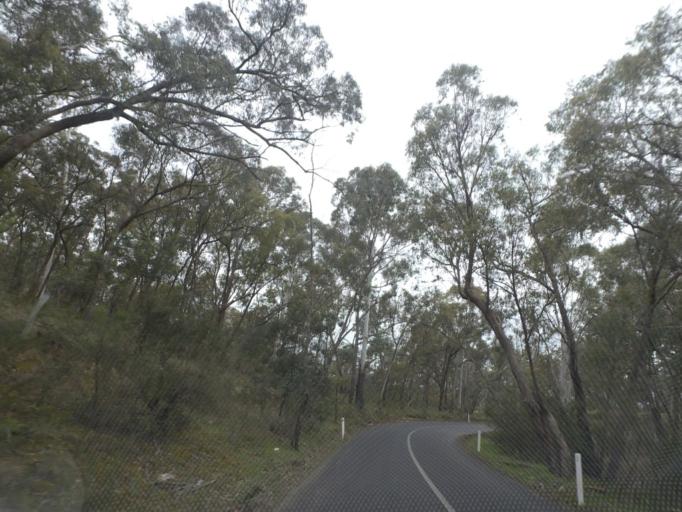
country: AU
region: Victoria
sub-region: Nillumbik
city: Hurstbridge
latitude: -37.6677
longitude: 145.2558
